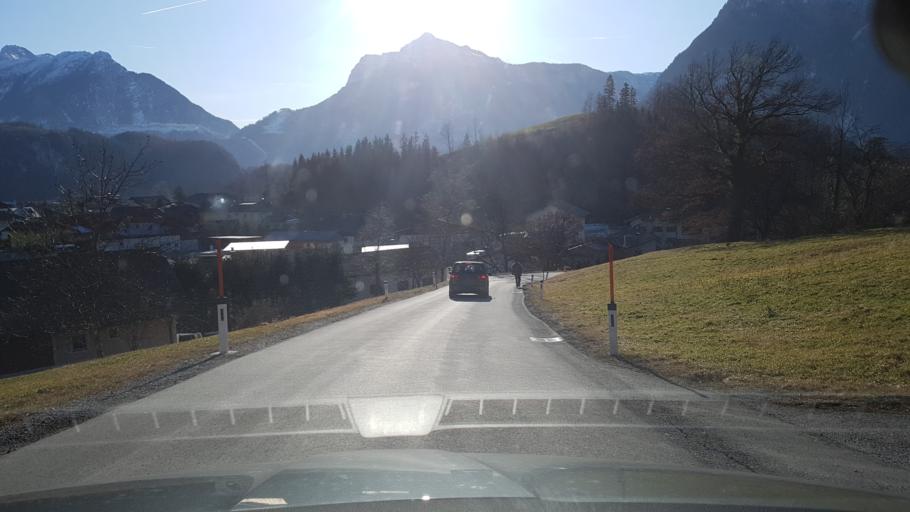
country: AT
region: Salzburg
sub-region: Politischer Bezirk Hallein
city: Golling an der Salzach
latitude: 47.6187
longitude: 13.1736
